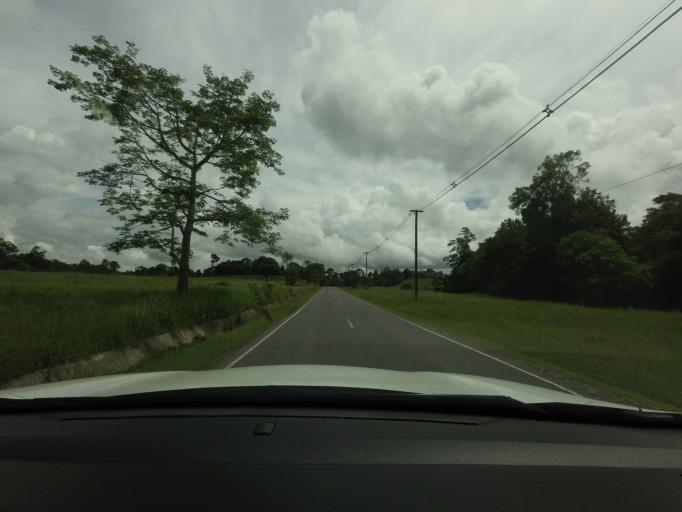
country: TH
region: Nakhon Nayok
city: Nakhon Nayok
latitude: 14.4175
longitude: 101.3713
